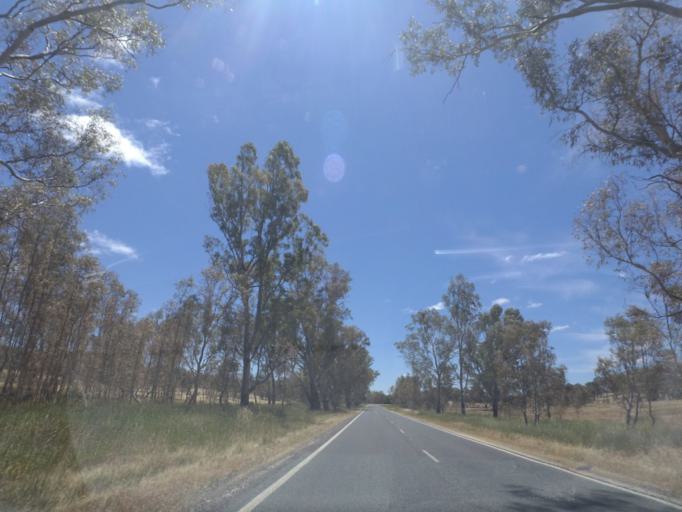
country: AU
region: Victoria
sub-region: Mount Alexander
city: Castlemaine
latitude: -37.1758
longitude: 144.1470
